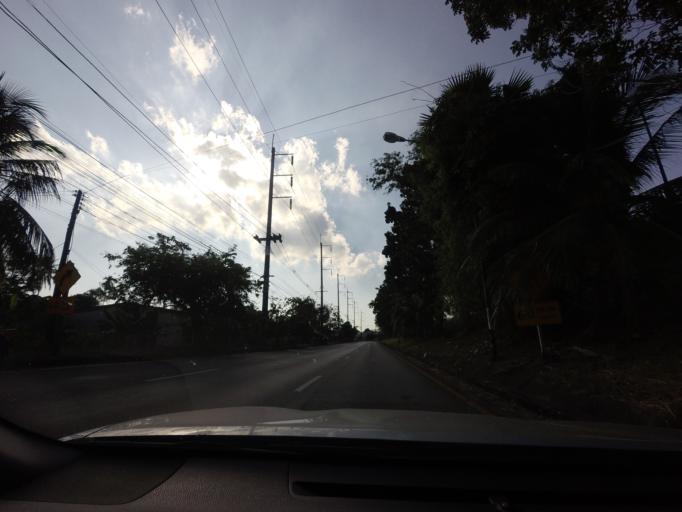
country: TH
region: Phangnga
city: Thai Mueang
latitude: 8.2702
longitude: 98.3201
